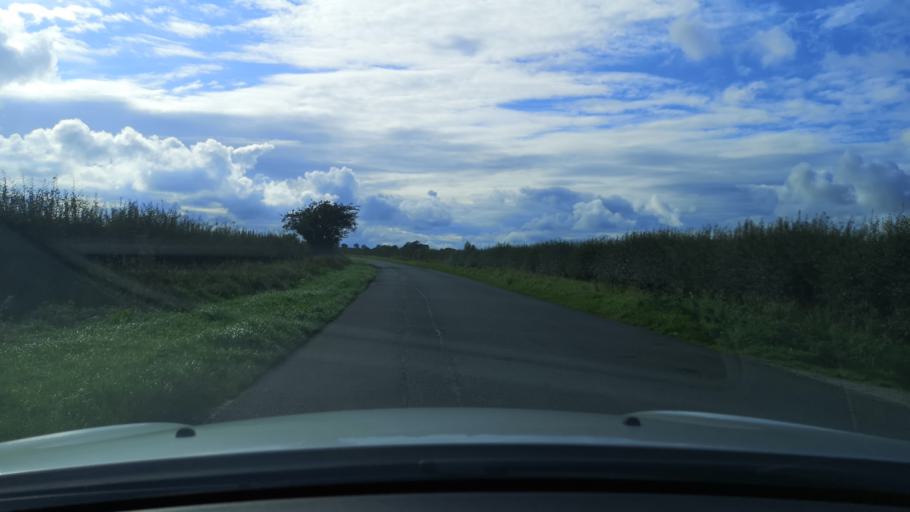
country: GB
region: England
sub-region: East Riding of Yorkshire
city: Walkington
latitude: 53.8286
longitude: -0.5089
